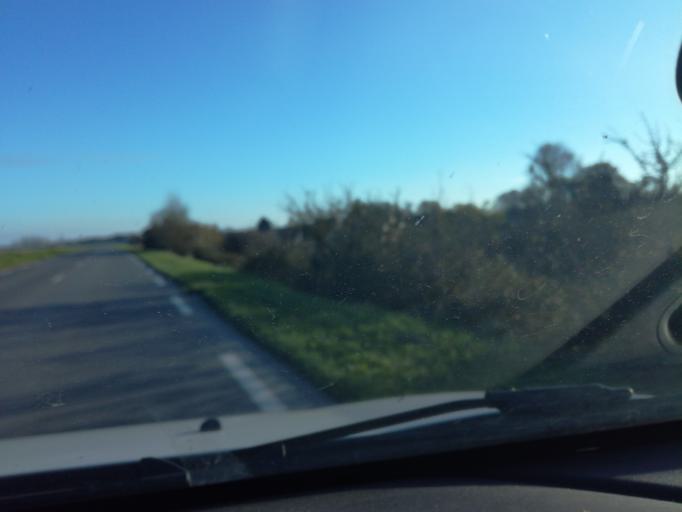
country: FR
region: Brittany
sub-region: Departement d'Ille-et-Vilaine
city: La Fresnais
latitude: 48.6278
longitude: -1.8611
